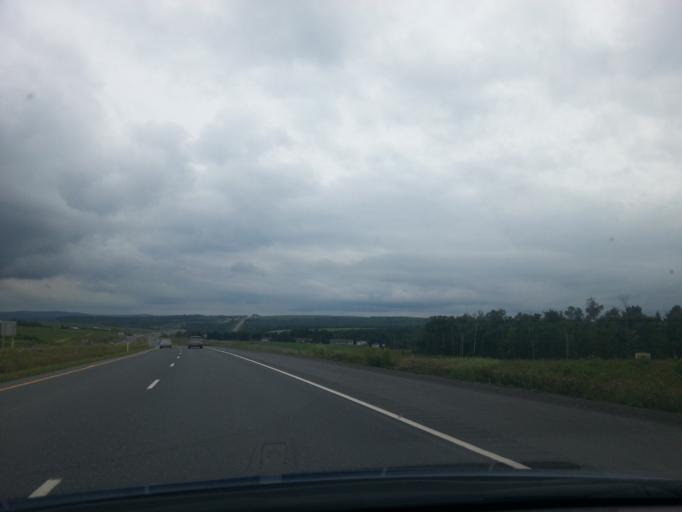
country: US
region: Maine
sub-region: Aroostook County
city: Limestone
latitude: 47.0288
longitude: -67.7671
